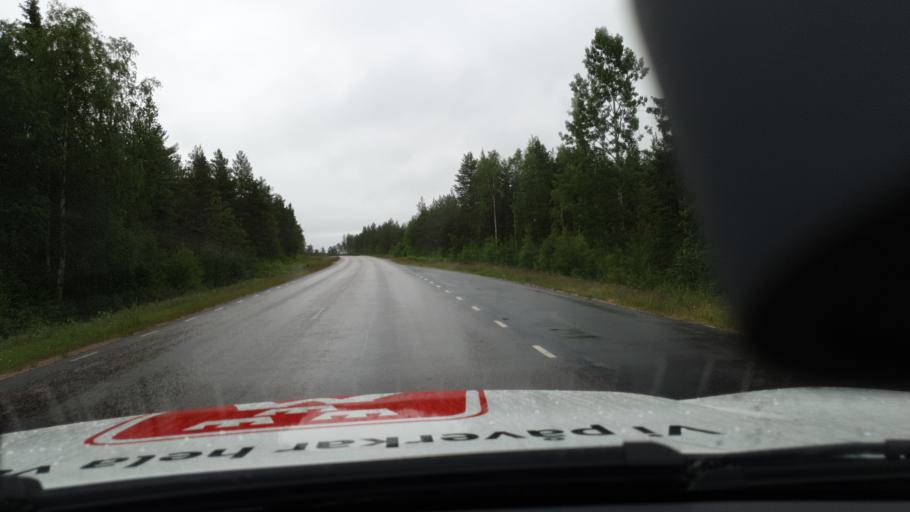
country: SE
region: Norrbotten
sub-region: Overtornea Kommun
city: OEvertornea
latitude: 66.4842
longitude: 23.7023
